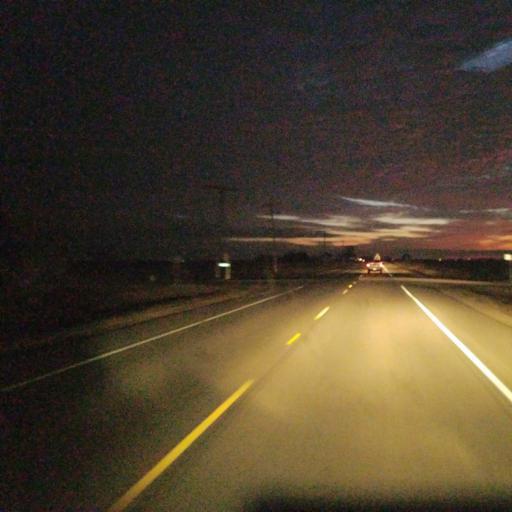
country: US
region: Illinois
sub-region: Peoria County
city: Hanna City
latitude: 40.6975
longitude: -89.8724
